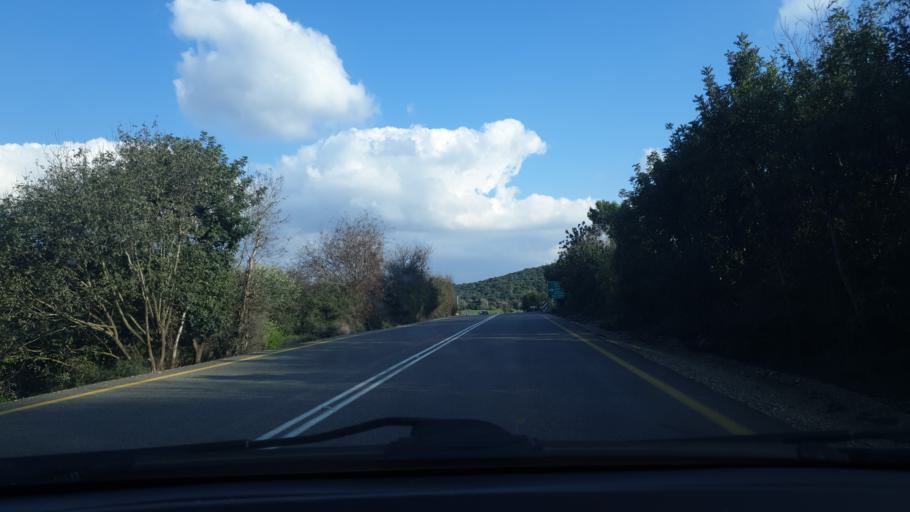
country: IL
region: Jerusalem
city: Bet Shemesh
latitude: 31.7038
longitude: 34.9391
